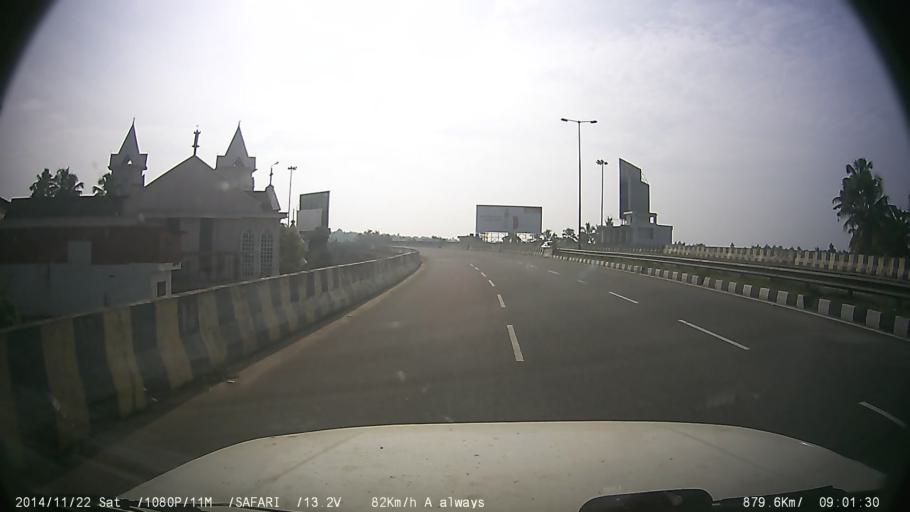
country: IN
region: Kerala
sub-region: Thrissur District
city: Kizhake Chalakudi
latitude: 10.3727
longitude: 76.3029
